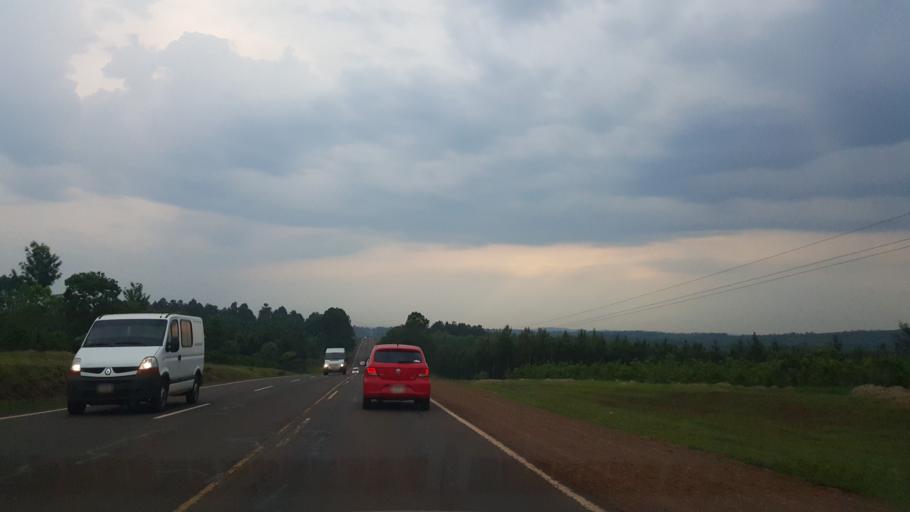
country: AR
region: Misiones
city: Gobernador Roca
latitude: -27.1649
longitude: -55.4387
